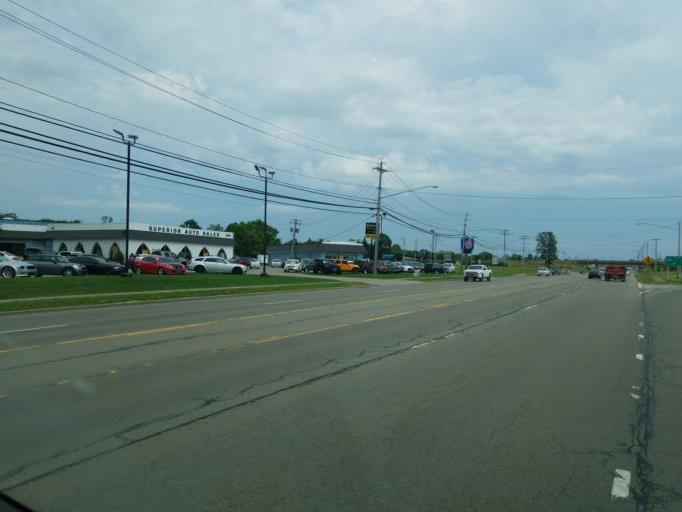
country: US
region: New York
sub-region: Erie County
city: Hamburg
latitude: 42.7456
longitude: -78.8515
